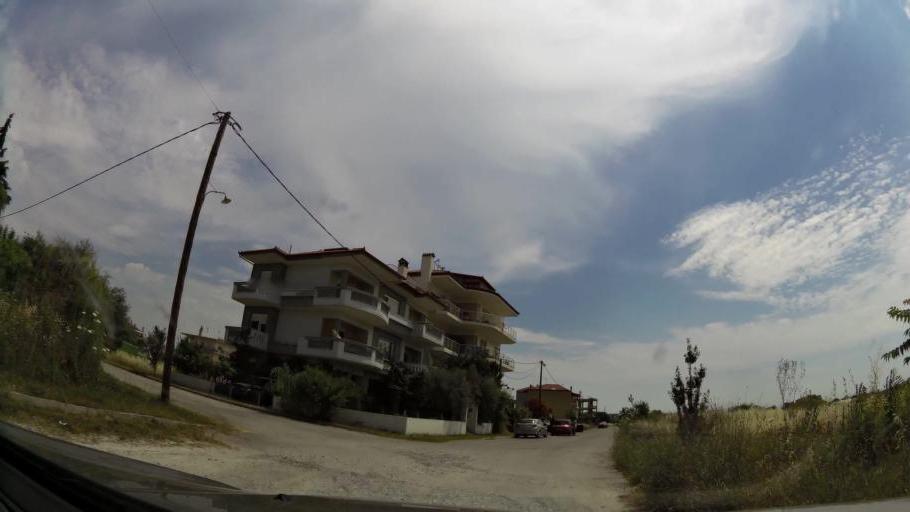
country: GR
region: Central Macedonia
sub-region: Nomos Pierias
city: Katerini
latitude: 40.2617
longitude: 22.5167
